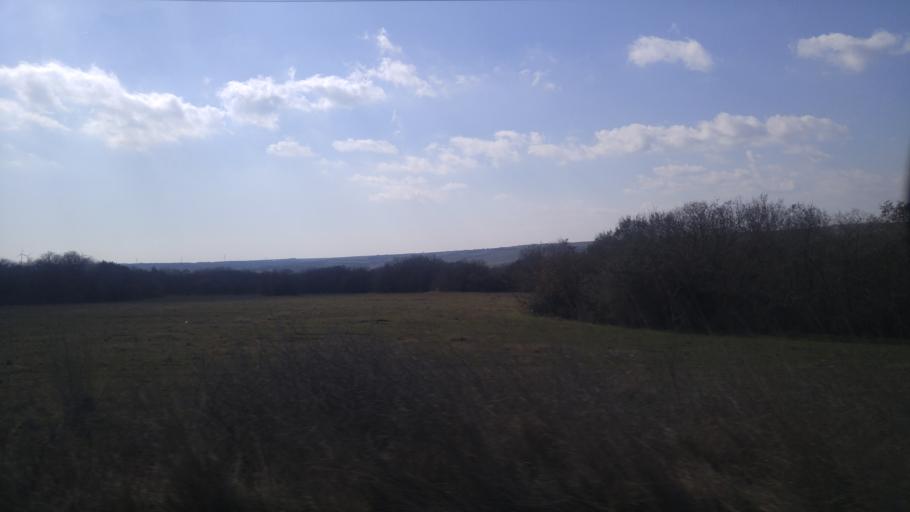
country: TR
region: Istanbul
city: Buyukcavuslu
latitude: 41.1904
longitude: 28.0829
